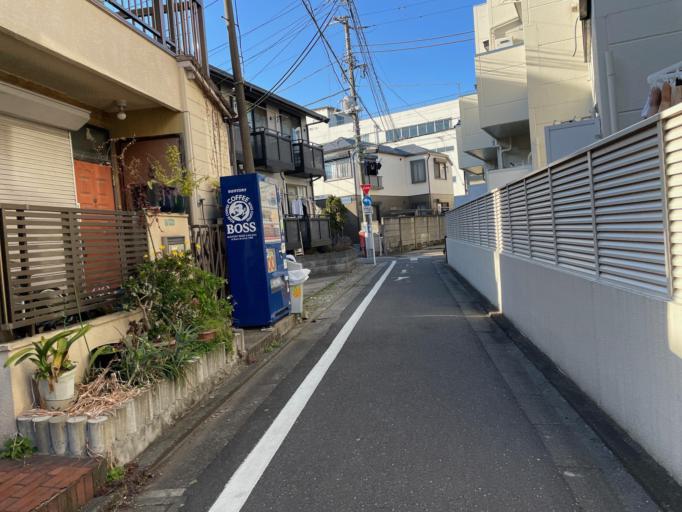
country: JP
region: Tokyo
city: Tokyo
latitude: 35.6315
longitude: 139.6959
